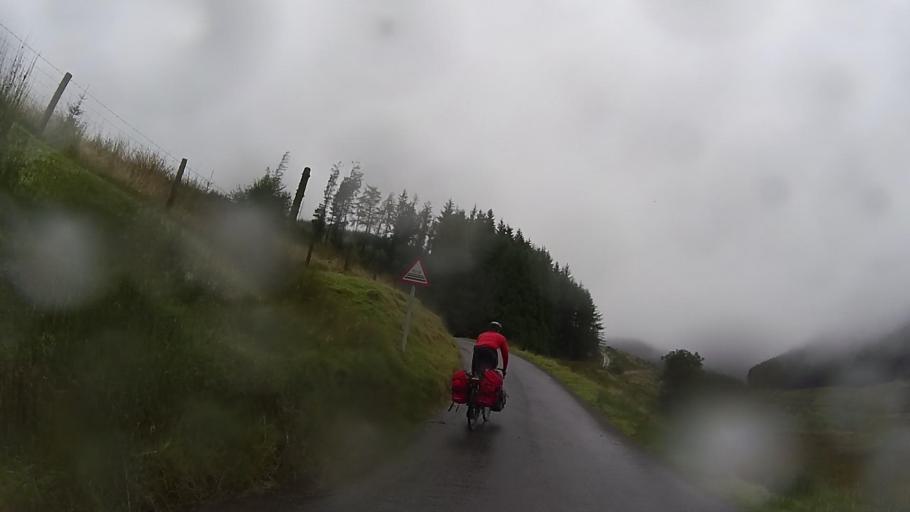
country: GB
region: Wales
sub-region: Carmarthenshire
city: Llandovery
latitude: 52.1867
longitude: -3.7102
